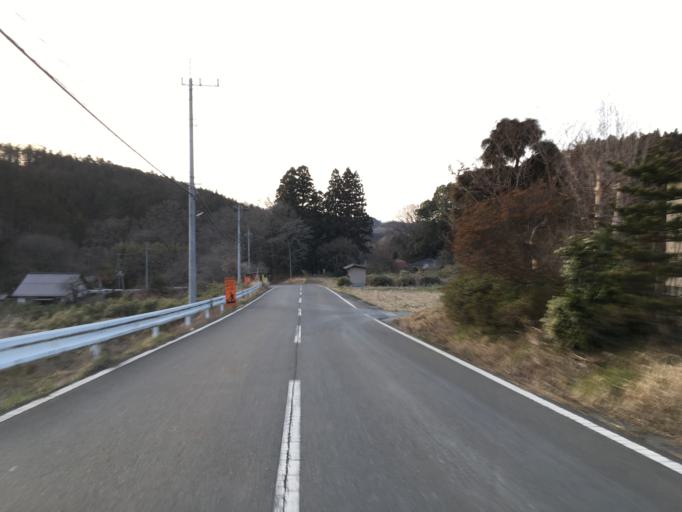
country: JP
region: Ibaraki
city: Daigo
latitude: 36.8053
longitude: 140.3810
